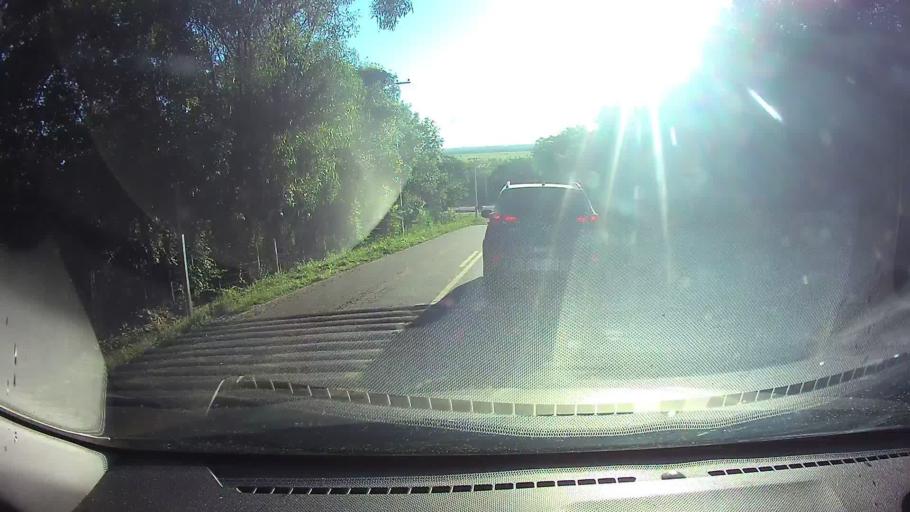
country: PY
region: Cordillera
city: Emboscada
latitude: -25.2075
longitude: -57.3518
